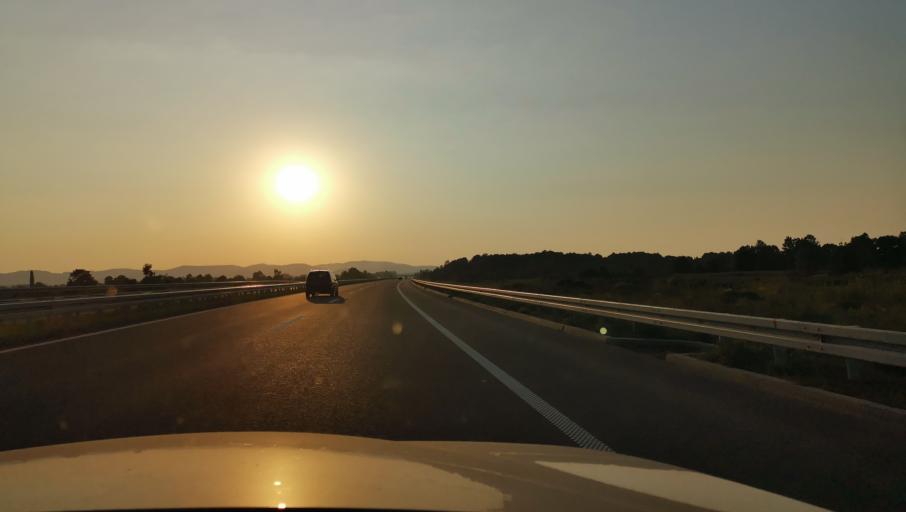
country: RS
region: Central Serbia
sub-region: Kolubarski Okrug
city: Lajkovac
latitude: 44.3476
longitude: 20.1712
